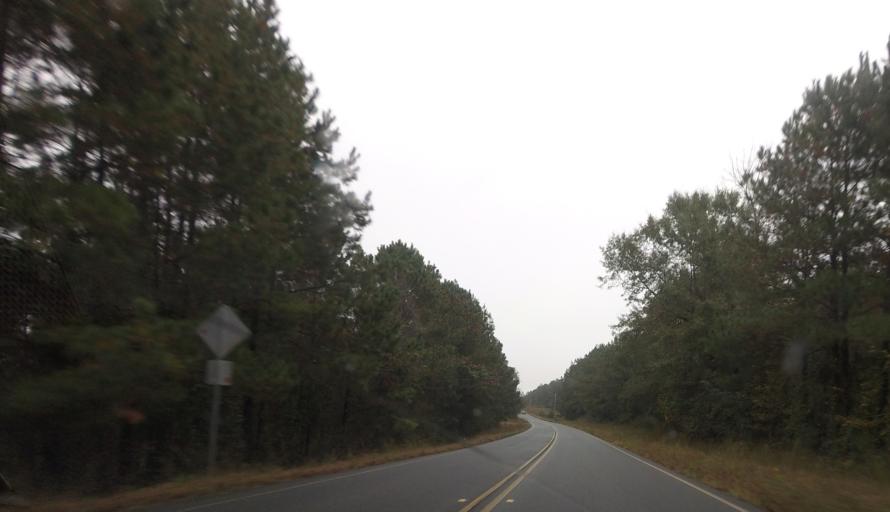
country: US
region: Georgia
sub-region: Marion County
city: Buena Vista
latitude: 32.3587
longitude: -84.4644
